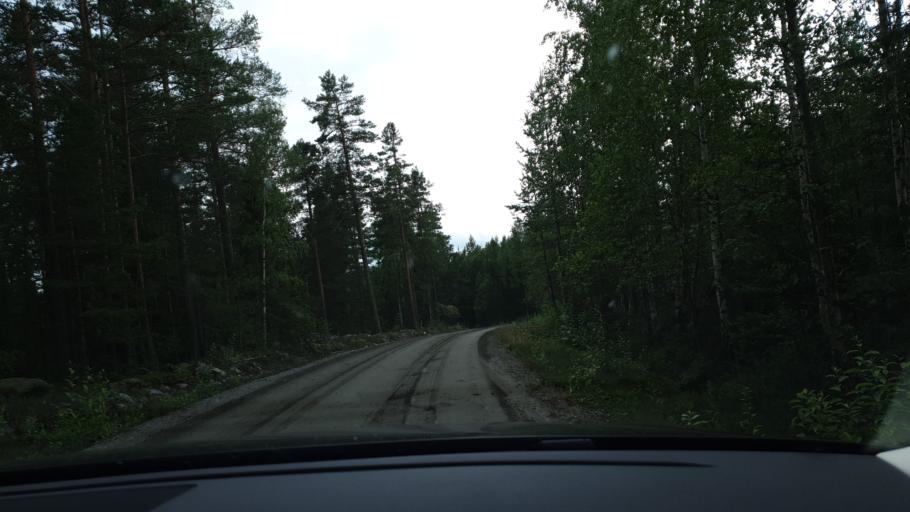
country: SE
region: Gaevleborg
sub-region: Hudiksvalls Kommun
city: Iggesund
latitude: 61.5192
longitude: 17.0169
